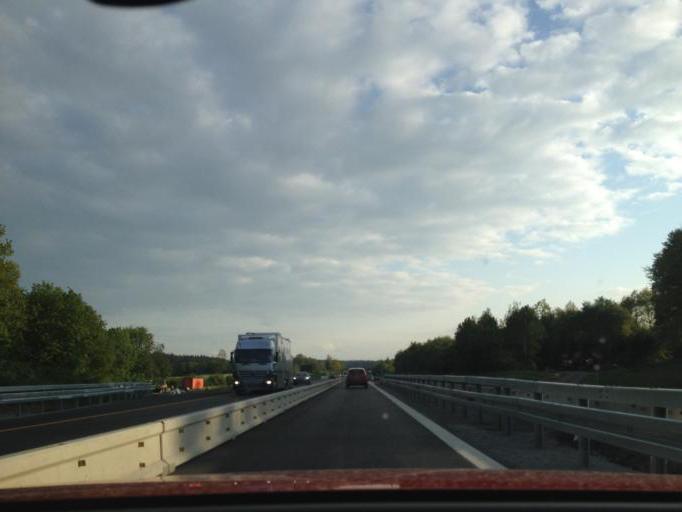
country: DE
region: Bavaria
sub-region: Upper Palatinate
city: Windischeschenbach
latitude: 49.7831
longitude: 12.1648
